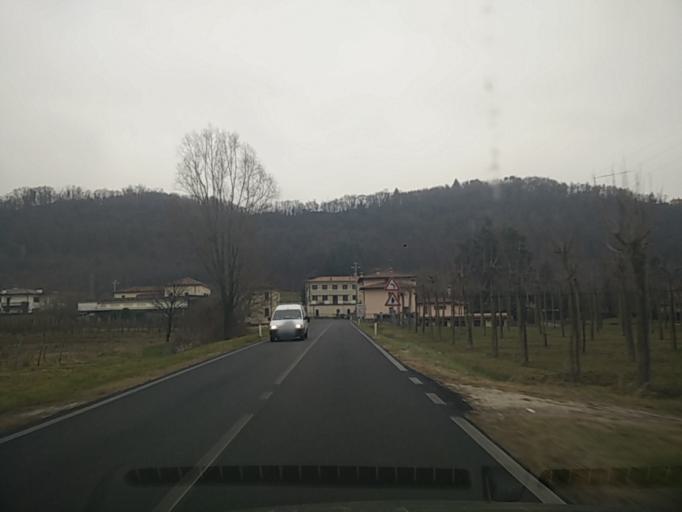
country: IT
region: Veneto
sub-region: Provincia di Treviso
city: Tarzo
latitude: 45.9781
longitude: 12.2146
